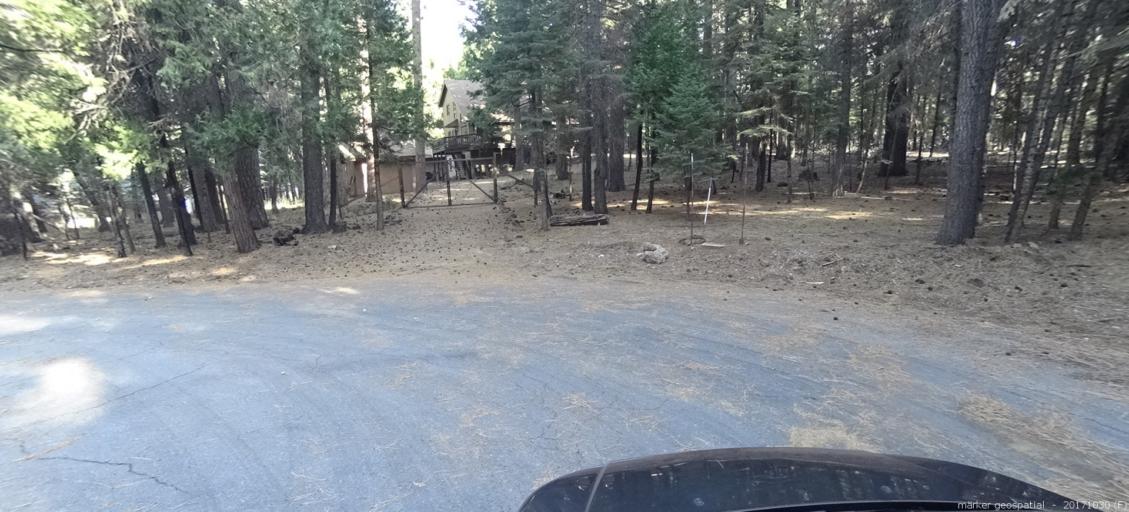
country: US
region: California
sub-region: Shasta County
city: Shingletown
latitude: 40.5516
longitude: -121.7352
